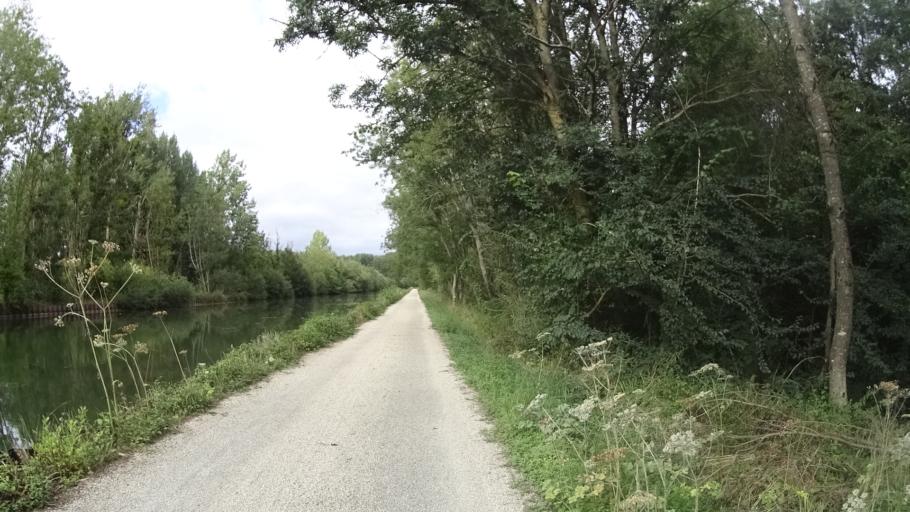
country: FR
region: Picardie
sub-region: Departement de l'Aisne
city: Itancourt
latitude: 49.7708
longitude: 3.3911
